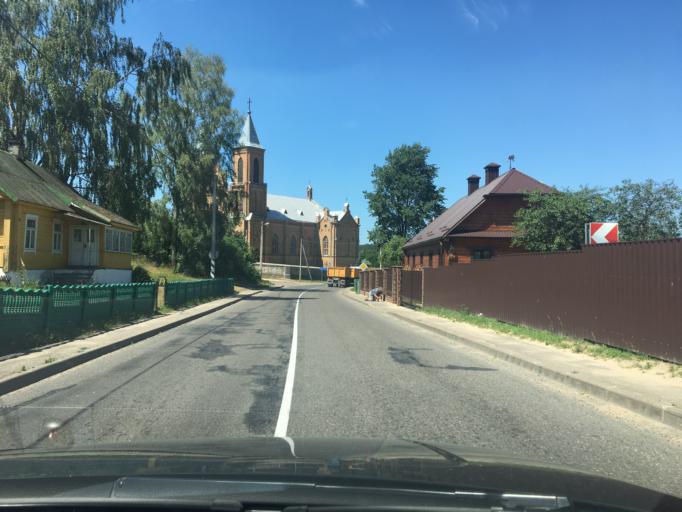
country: BY
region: Grodnenskaya
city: Hal'shany
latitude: 54.1549
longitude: 25.9087
